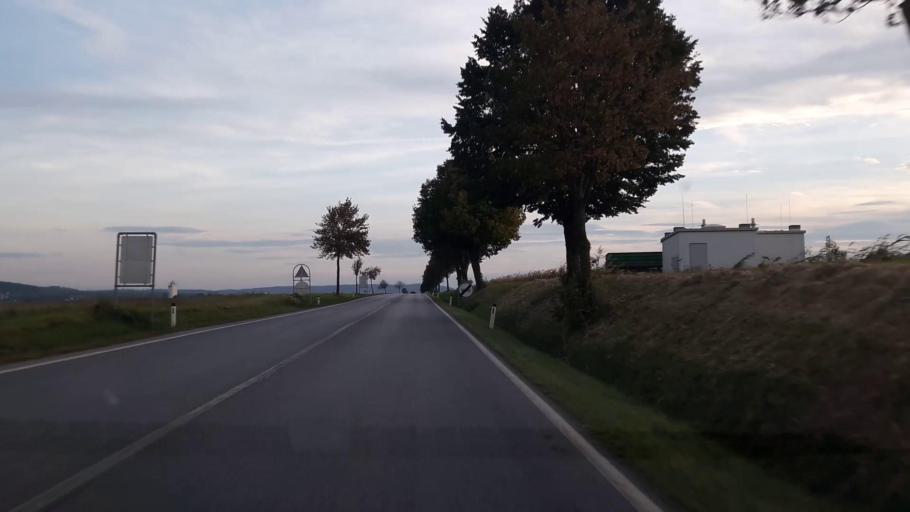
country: AT
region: Lower Austria
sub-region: Politischer Bezirk Korneuburg
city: Harmannsdorf
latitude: 48.4077
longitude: 16.3775
